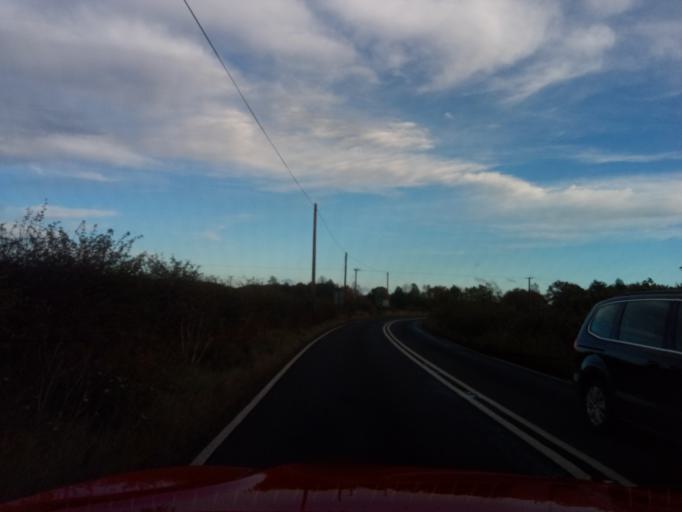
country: GB
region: England
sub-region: Northumberland
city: Ford
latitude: 55.6227
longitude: -2.1211
